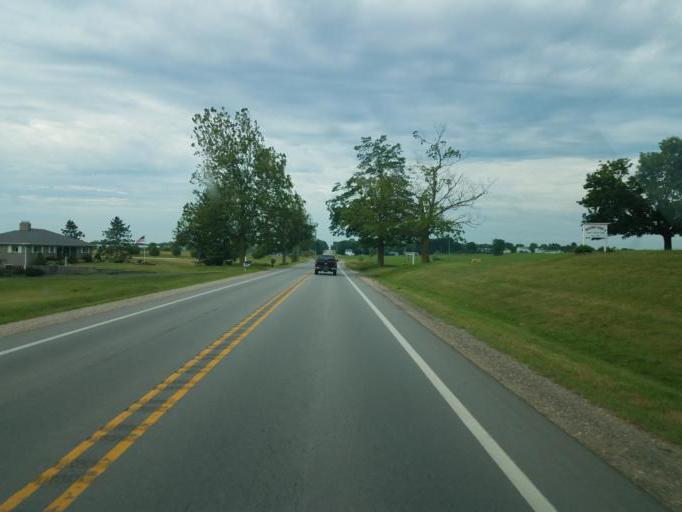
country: US
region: Michigan
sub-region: Eaton County
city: Charlotte
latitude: 42.5899
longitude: -84.8361
